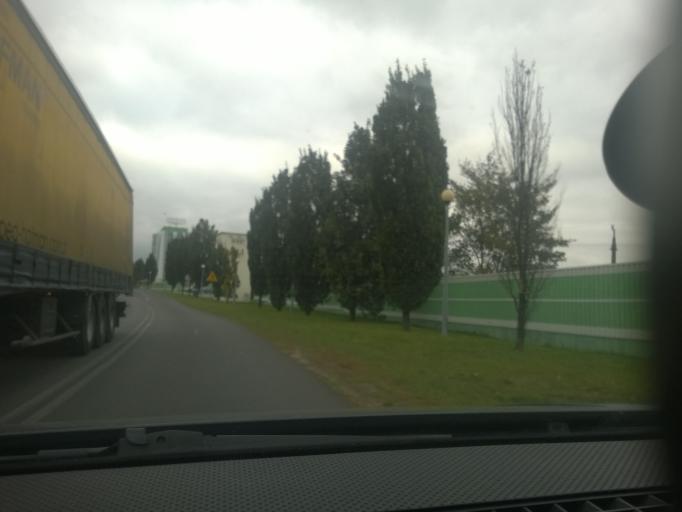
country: PL
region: Greater Poland Voivodeship
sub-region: Powiat kaliski
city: Opatowek
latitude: 51.7337
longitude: 18.1918
